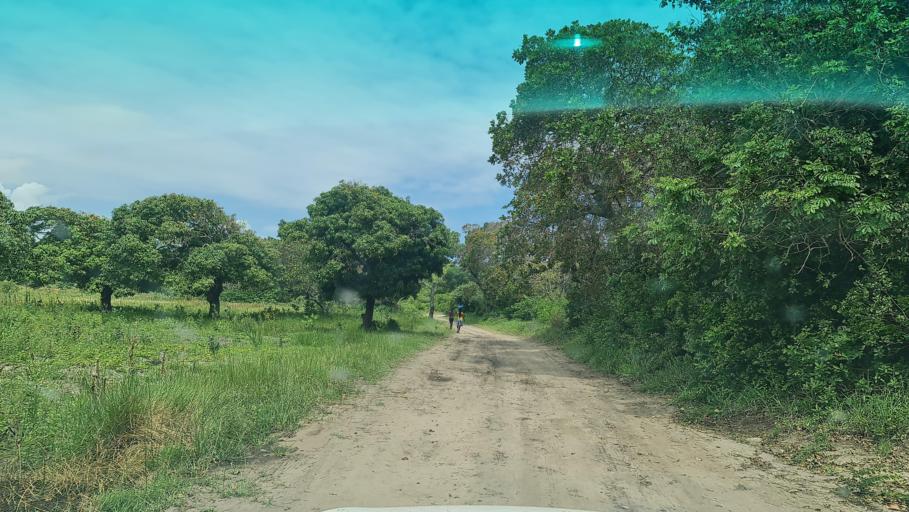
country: MZ
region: Maputo
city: Manhica
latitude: -25.5197
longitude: 32.8688
